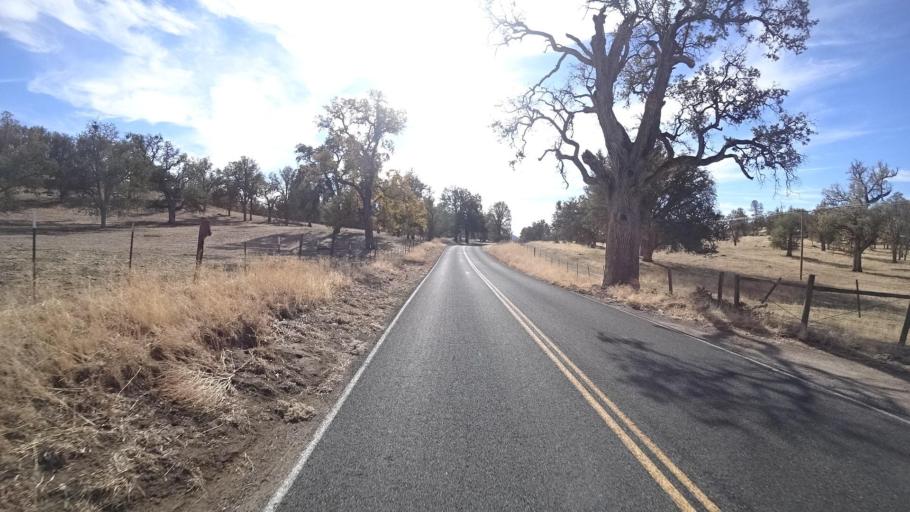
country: US
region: California
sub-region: Kern County
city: Alta Sierra
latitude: 35.7000
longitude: -118.7303
